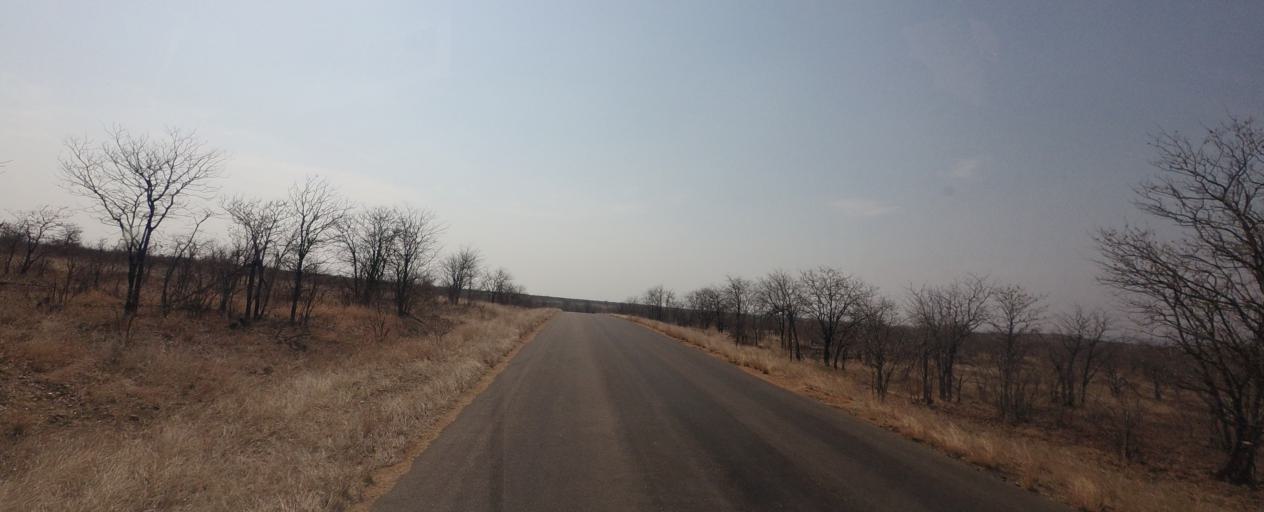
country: ZA
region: Limpopo
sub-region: Mopani District Municipality
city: Phalaborwa
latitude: -23.9493
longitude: 31.6172
